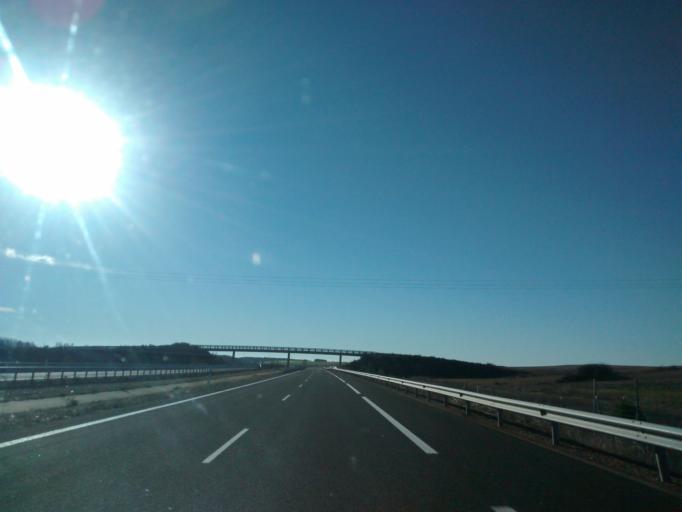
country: ES
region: Castille and Leon
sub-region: Provincia de Palencia
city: Espinosa de Villagonzalo
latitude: 42.4757
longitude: -4.3857
